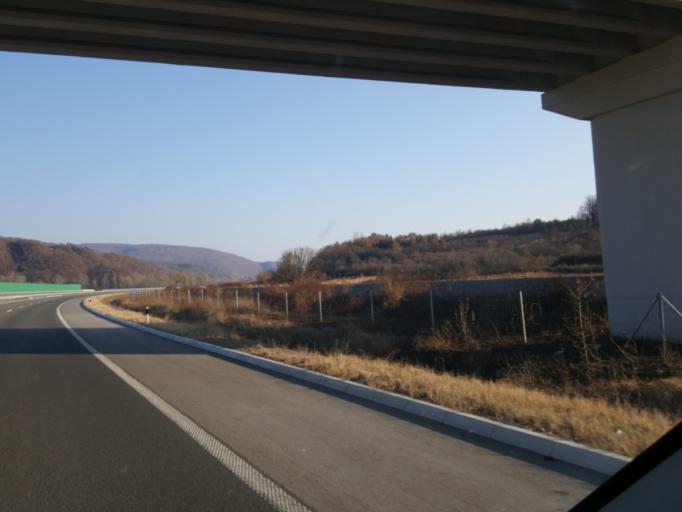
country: RS
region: Central Serbia
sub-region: Pirotski Okrug
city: Dimitrovgrad
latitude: 43.0592
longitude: 22.6902
